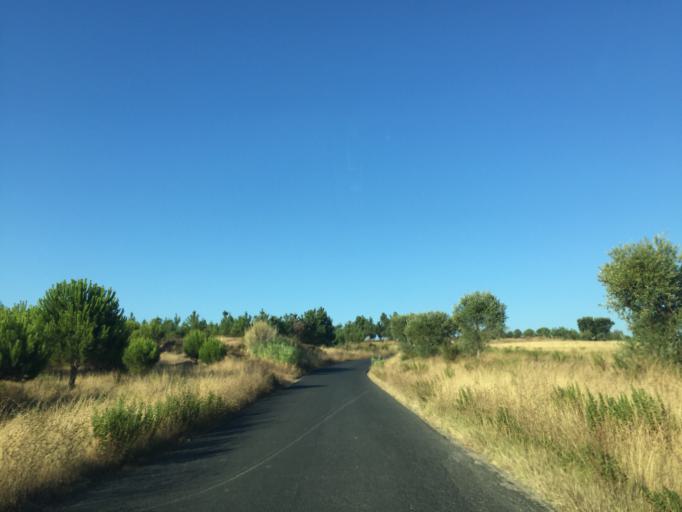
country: PT
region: Lisbon
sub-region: Azambuja
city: Aveiras de Cima
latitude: 39.1348
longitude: -8.9366
